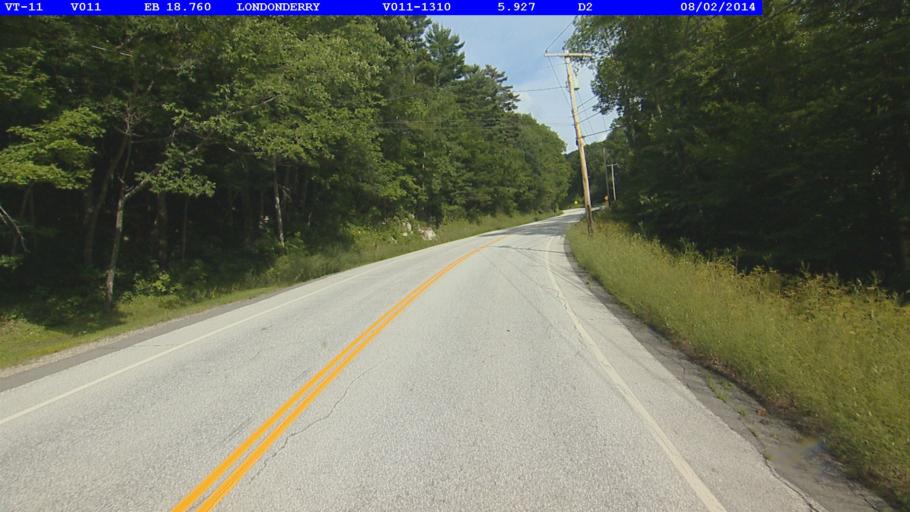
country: US
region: Vermont
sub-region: Windsor County
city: Chester
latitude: 43.2151
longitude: -72.7523
